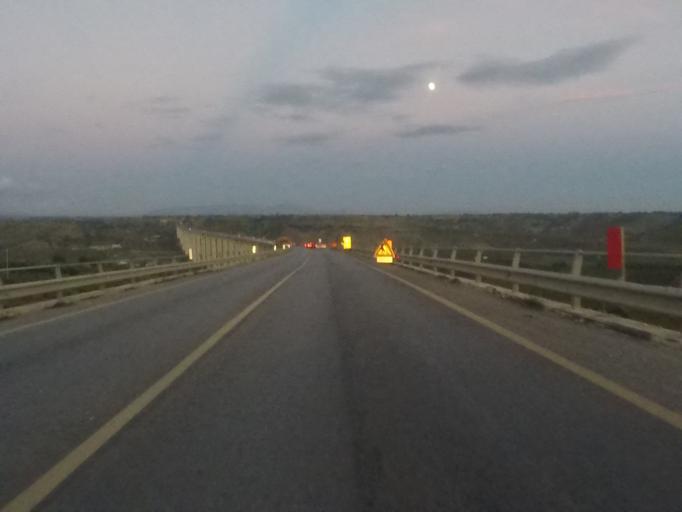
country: IT
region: Sicily
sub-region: Trapani
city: Marinella
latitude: 37.6333
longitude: 12.8763
